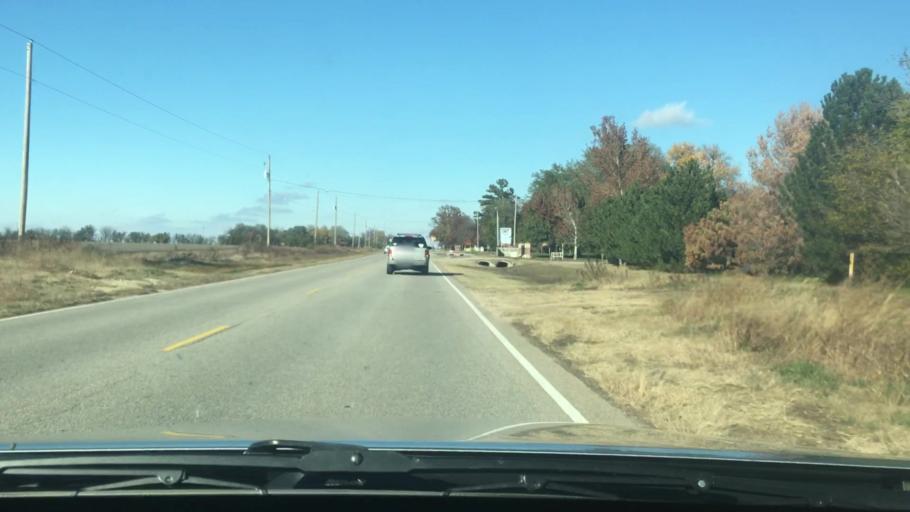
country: US
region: Kansas
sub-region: Sedgwick County
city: Maize
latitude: 37.7616
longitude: -97.4808
